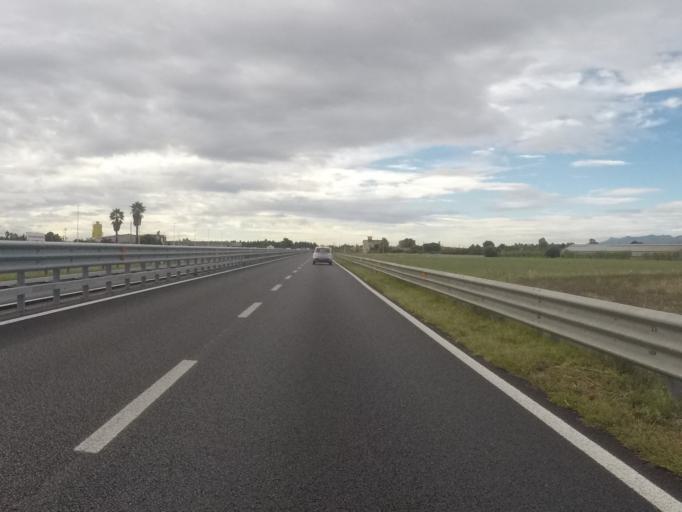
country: IT
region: Sardinia
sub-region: Provincia di Cagliari
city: Decimomannu
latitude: 39.3124
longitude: 8.9815
